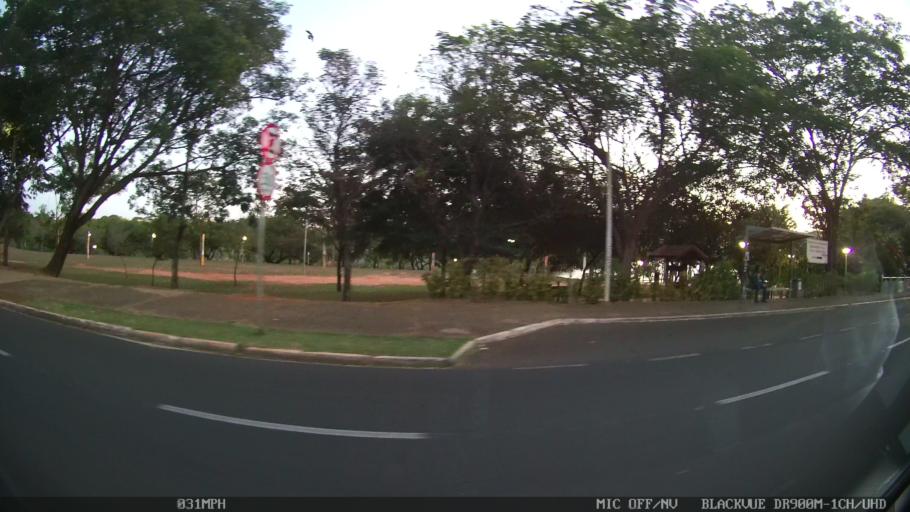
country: BR
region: Sao Paulo
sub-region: Sao Jose Do Rio Preto
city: Sao Jose do Rio Preto
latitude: -20.8071
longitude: -49.3598
